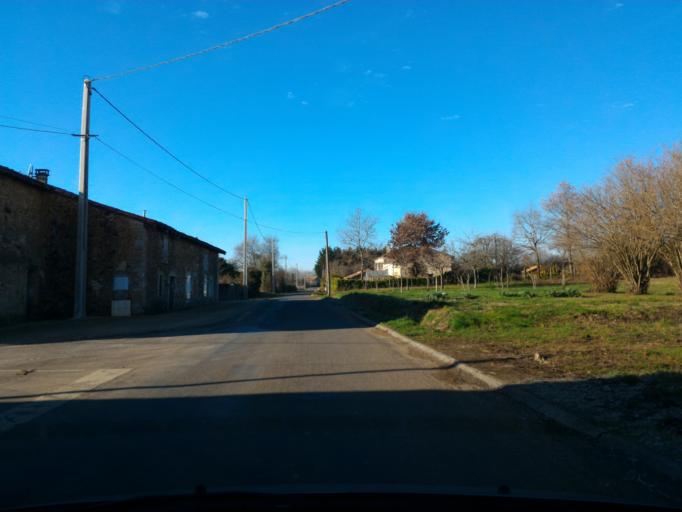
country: FR
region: Poitou-Charentes
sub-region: Departement de la Charente
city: Nanteuil-en-Vallee
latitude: 45.9555
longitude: 0.3549
